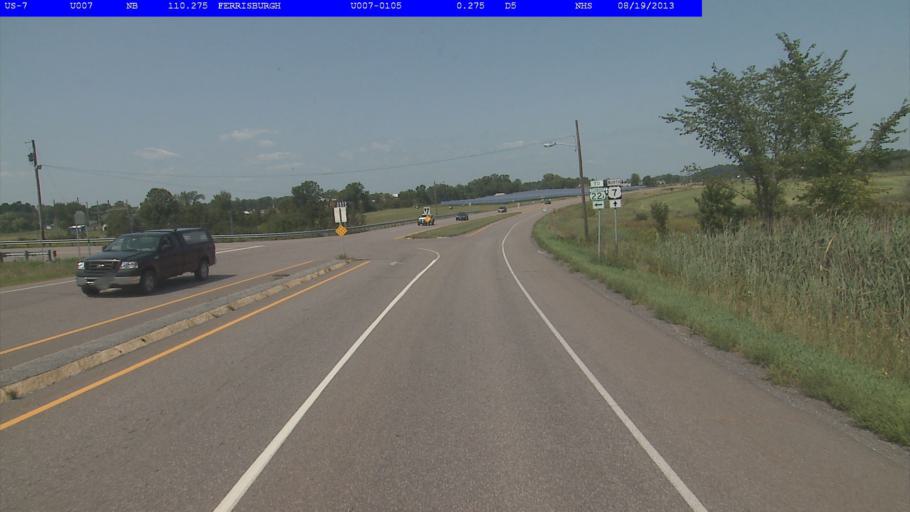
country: US
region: Vermont
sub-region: Addison County
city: Vergennes
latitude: 44.1658
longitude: -73.2385
